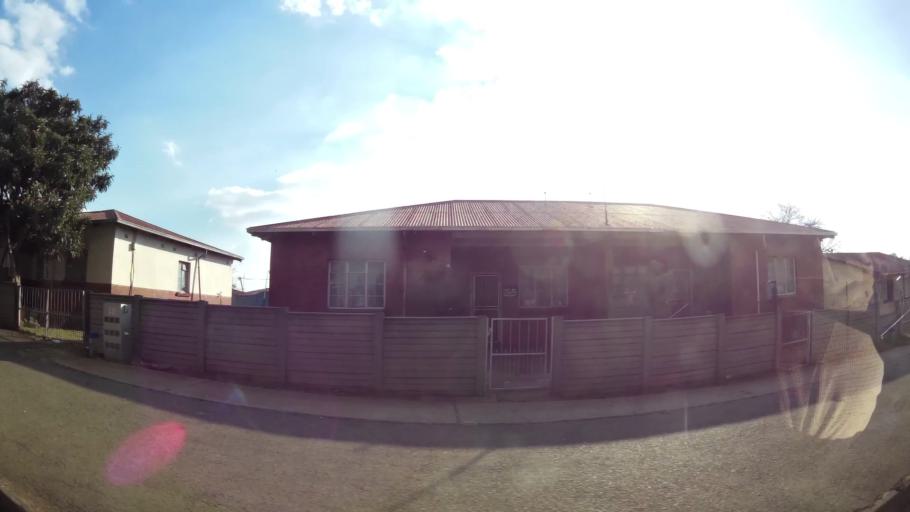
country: ZA
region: Gauteng
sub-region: West Rand District Municipality
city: Krugersdorp
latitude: -26.0959
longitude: 27.7558
